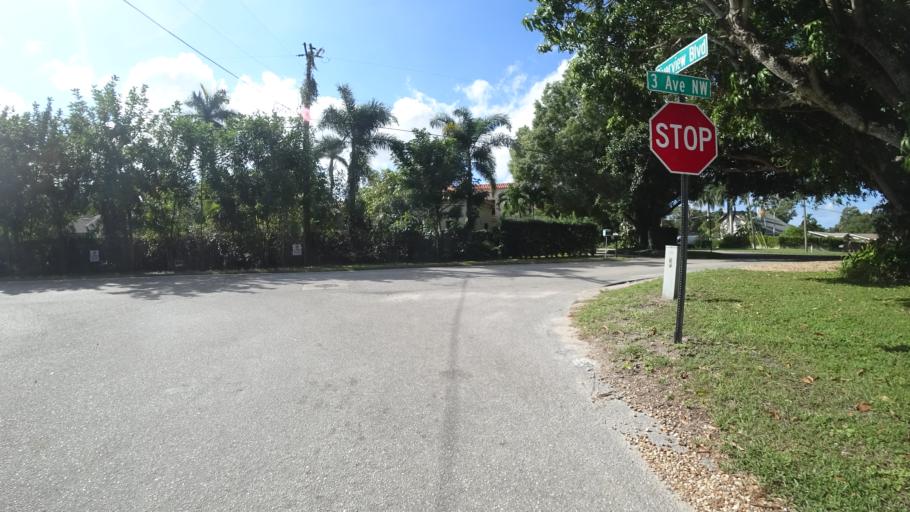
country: US
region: Florida
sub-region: Manatee County
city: West Bradenton
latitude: 27.5012
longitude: -82.6006
